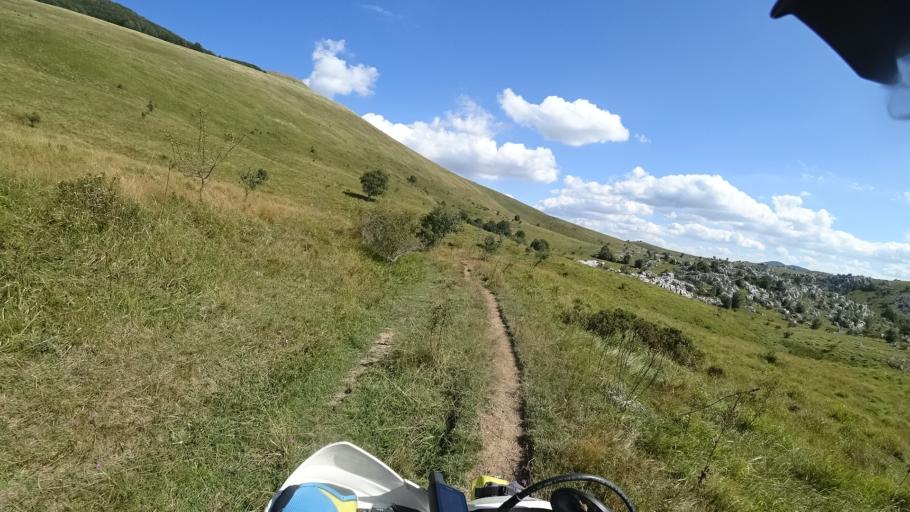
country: HR
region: Zadarska
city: Gracac
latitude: 44.4054
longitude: 16.0048
